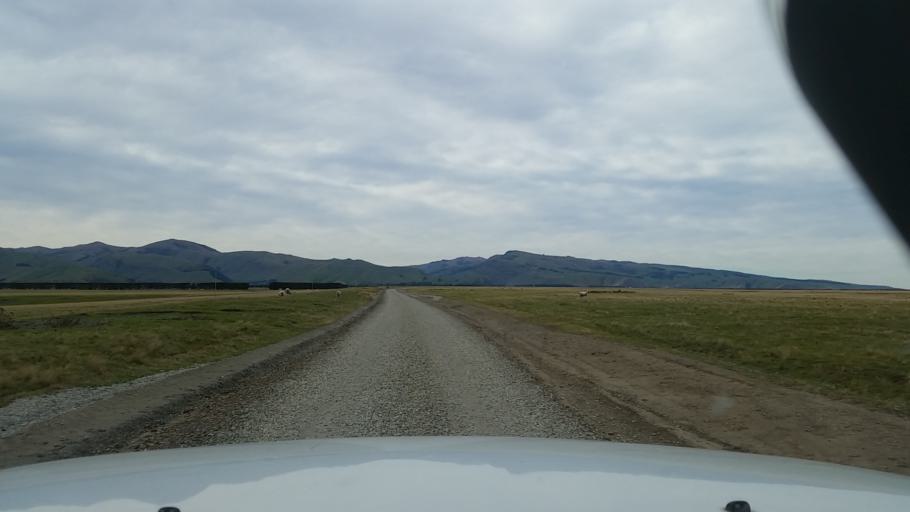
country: NZ
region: Canterbury
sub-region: Selwyn District
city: Lincoln
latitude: -43.8181
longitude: 172.6130
